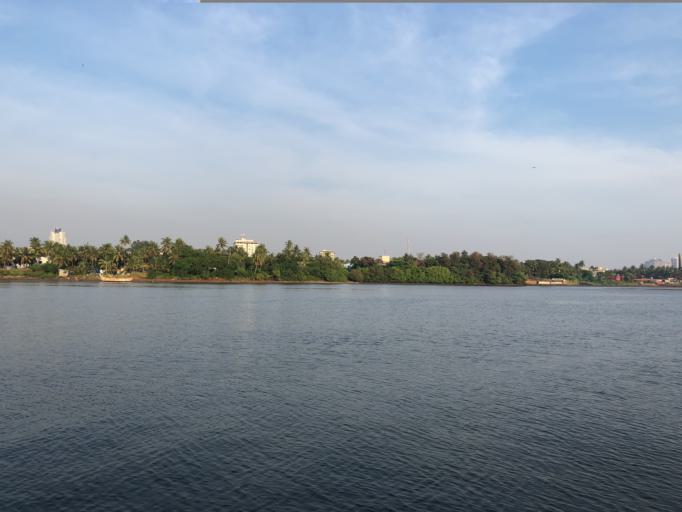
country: IN
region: Karnataka
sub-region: Dakshina Kannada
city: Mangalore
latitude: 12.8852
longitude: 74.8192
